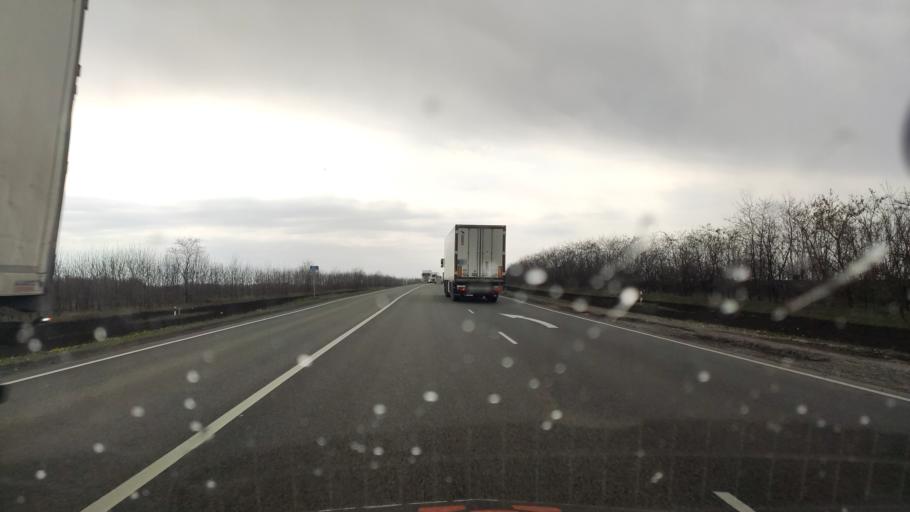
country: RU
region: Voronezj
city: Nizhnedevitsk
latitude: 51.5655
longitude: 38.3495
